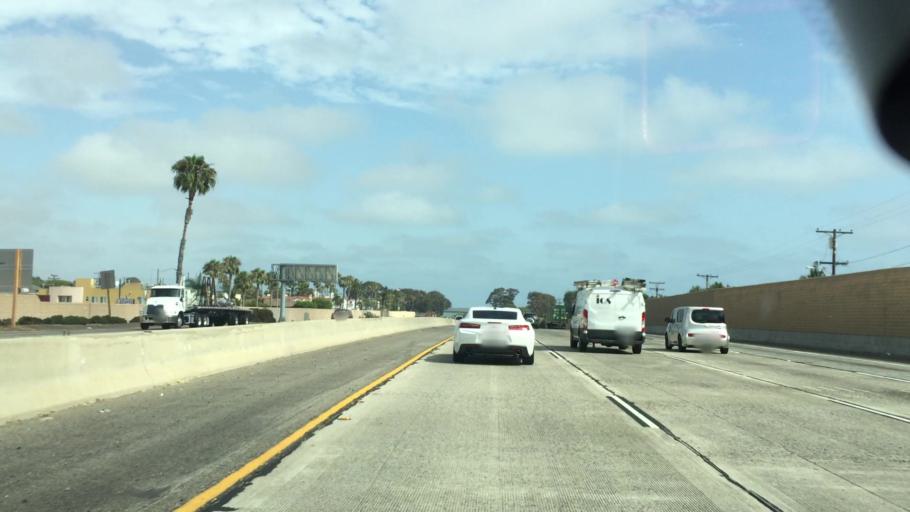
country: US
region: California
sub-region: Orange County
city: San Clemente
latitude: 33.4026
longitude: -117.5969
